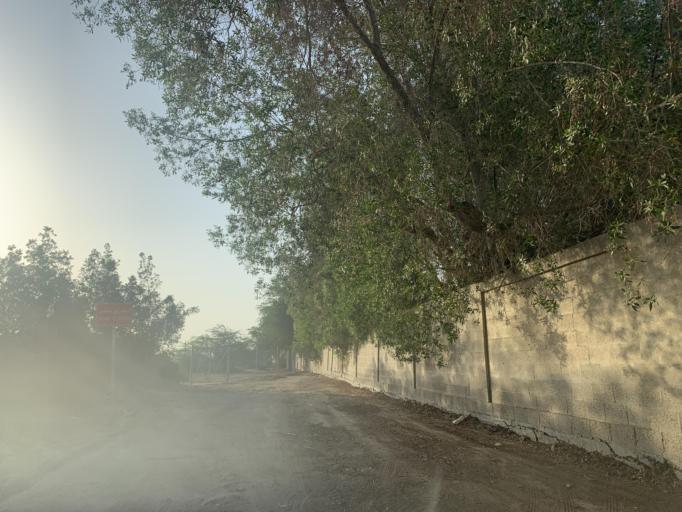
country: BH
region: Manama
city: Jidd Hafs
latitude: 26.2219
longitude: 50.5278
